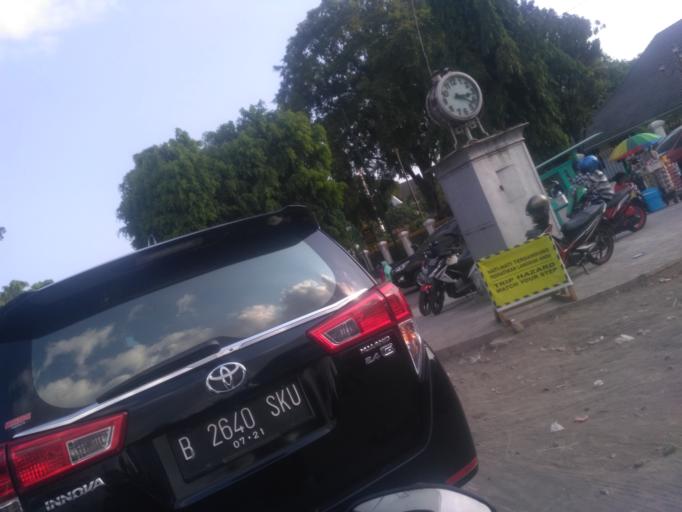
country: ID
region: Daerah Istimewa Yogyakarta
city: Yogyakarta
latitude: -7.7995
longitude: 110.3650
